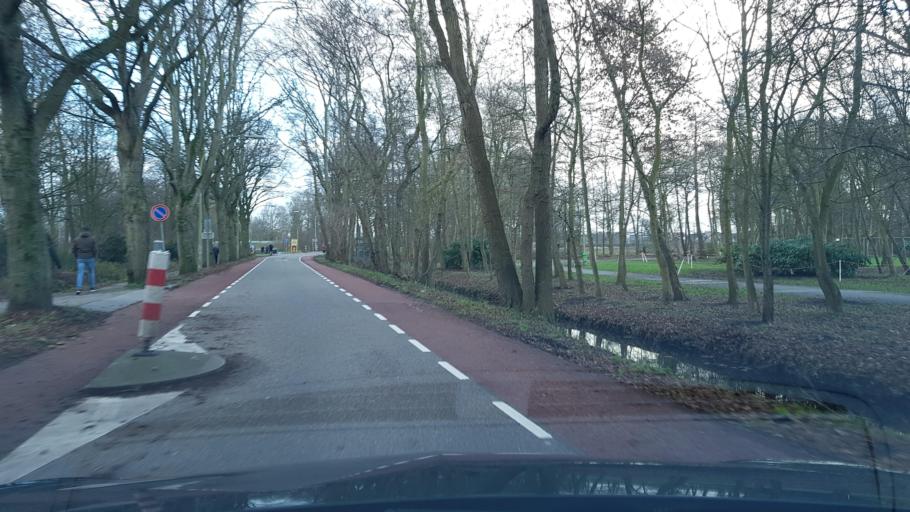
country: NL
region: South Holland
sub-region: Gemeente Lisse
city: Lisse
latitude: 52.2579
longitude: 4.5435
